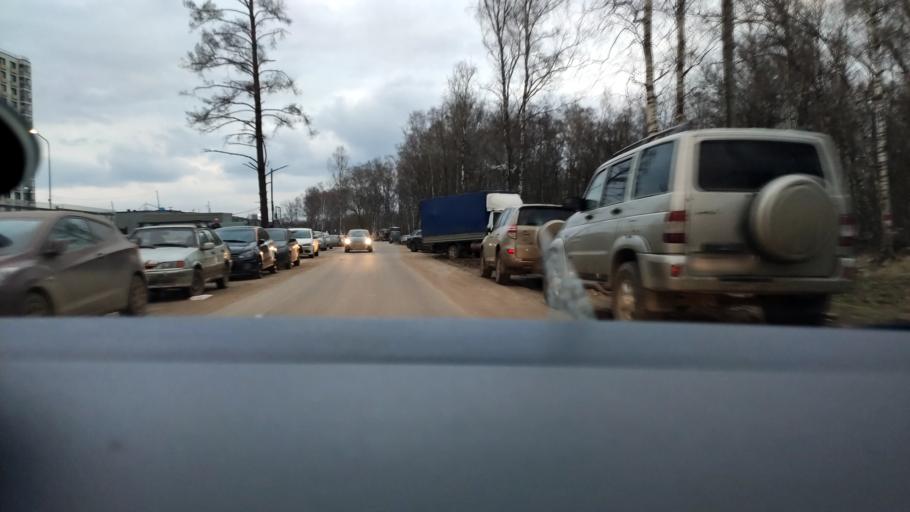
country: RU
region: Moskovskaya
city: Kommunarka
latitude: 55.5534
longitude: 37.4676
